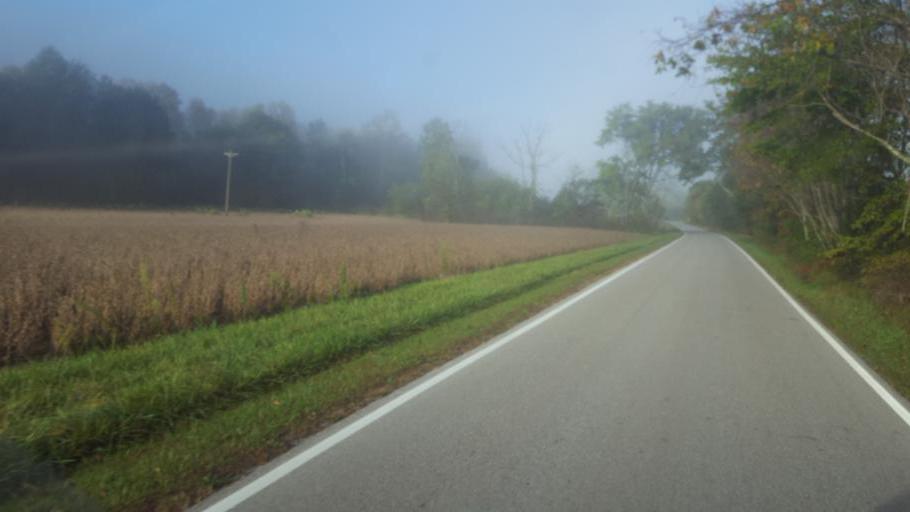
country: US
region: Ohio
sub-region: Adams County
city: Manchester
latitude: 38.5096
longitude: -83.5359
